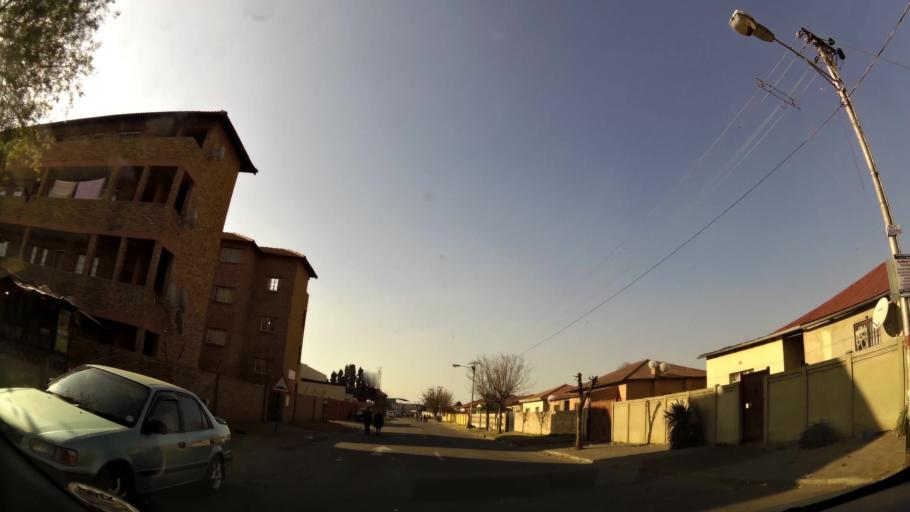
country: ZA
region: Gauteng
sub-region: West Rand District Municipality
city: Randfontein
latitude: -26.1844
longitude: 27.6972
